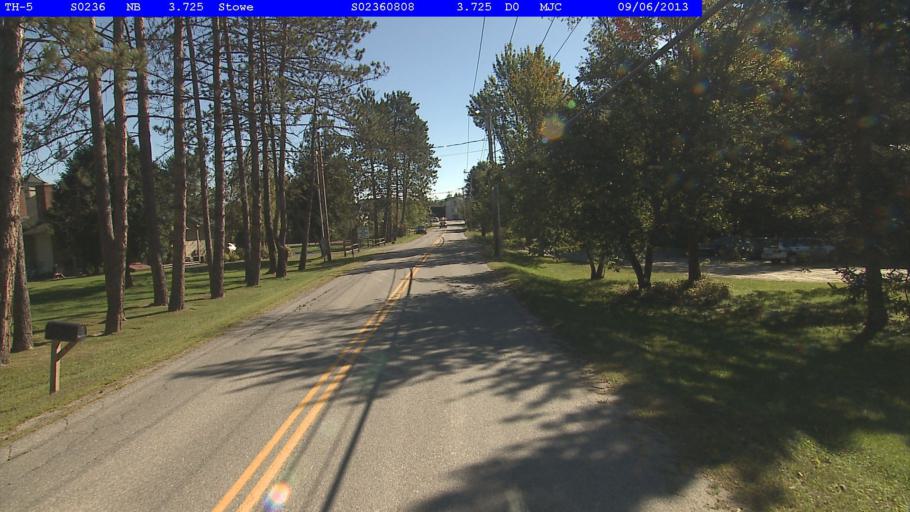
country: US
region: Vermont
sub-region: Lamoille County
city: Morristown
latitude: 44.4739
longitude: -72.7186
